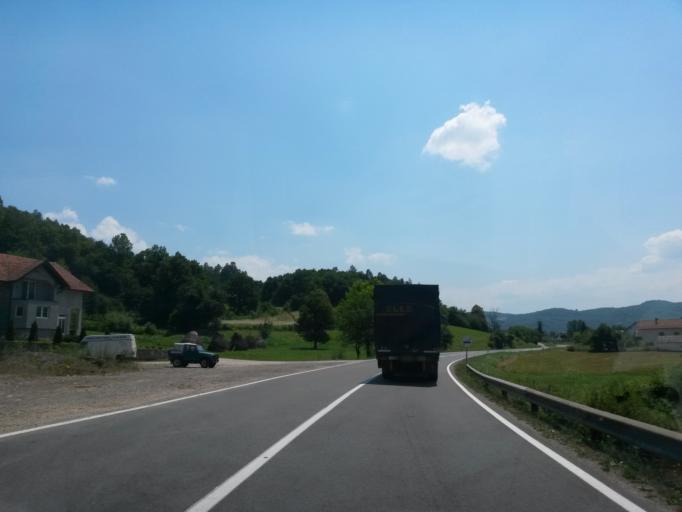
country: BA
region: Federation of Bosnia and Herzegovina
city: Lijesnica
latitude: 44.4988
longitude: 18.0816
